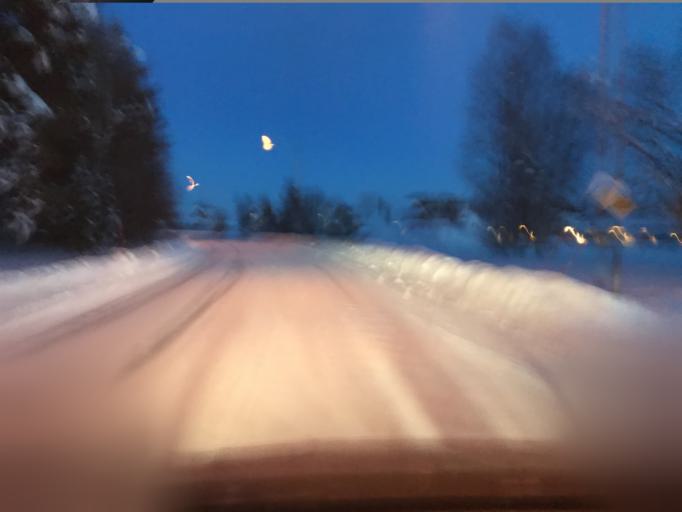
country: SE
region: Norrbotten
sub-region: Lulea Kommun
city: Sodra Sunderbyn
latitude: 65.6505
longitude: 21.9567
